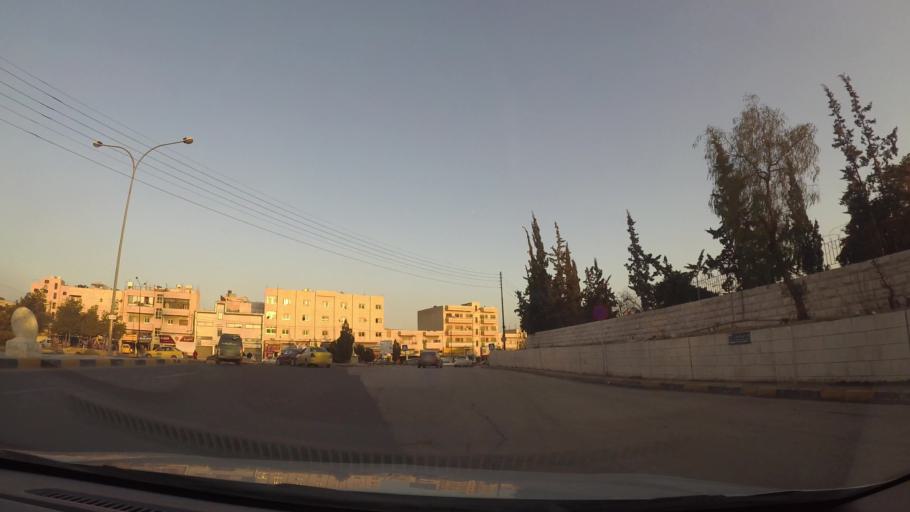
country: JO
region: Amman
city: Al Quwaysimah
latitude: 31.9049
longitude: 35.9364
